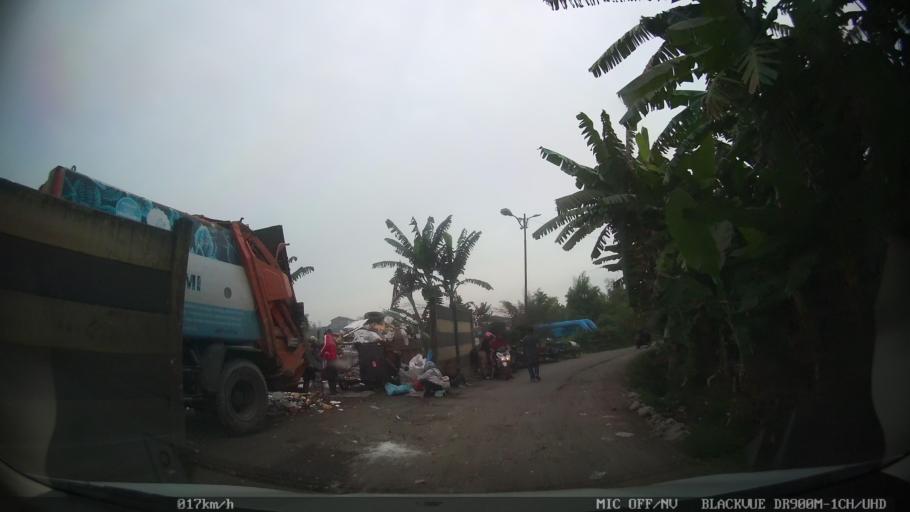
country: ID
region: North Sumatra
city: Deli Tua
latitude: 3.5479
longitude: 98.7156
